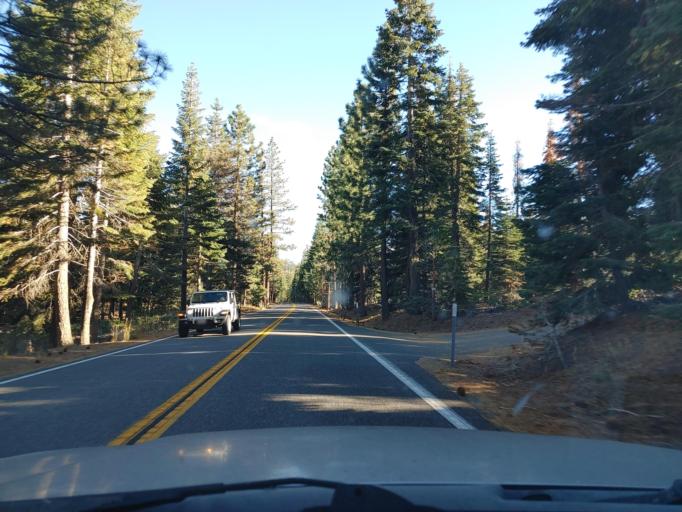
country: US
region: California
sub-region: Placer County
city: Tahoma
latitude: 39.0063
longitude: -120.1166
